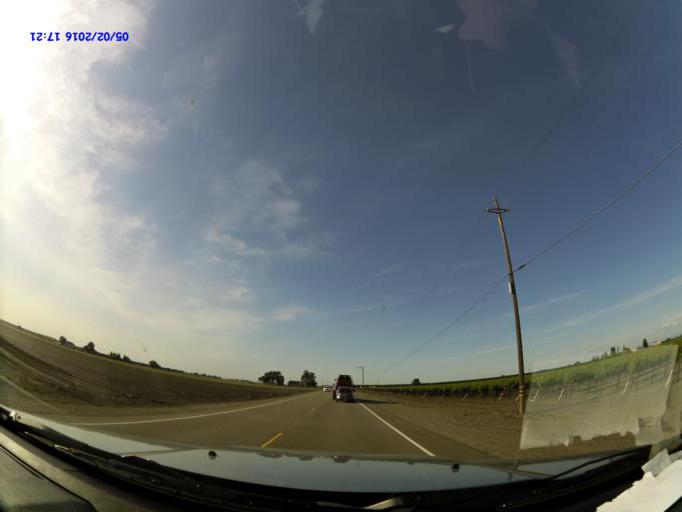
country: US
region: California
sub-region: San Joaquin County
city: Manteca
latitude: 37.8486
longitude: -121.1453
